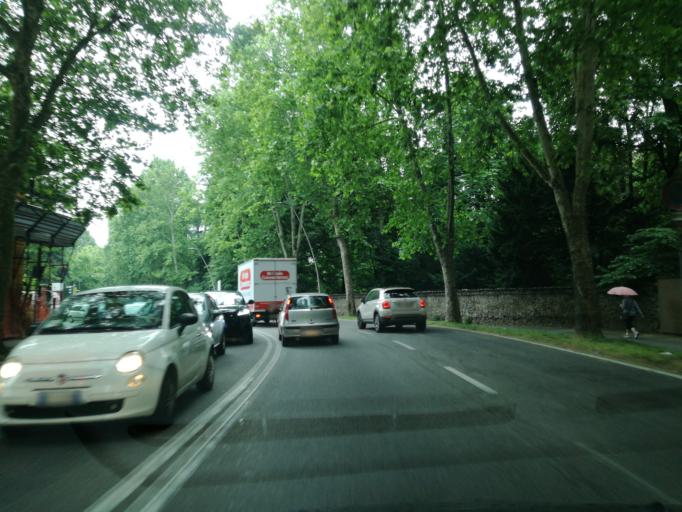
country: IT
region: Lombardy
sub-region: Provincia di Monza e Brianza
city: Monza
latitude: 45.5917
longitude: 9.2721
